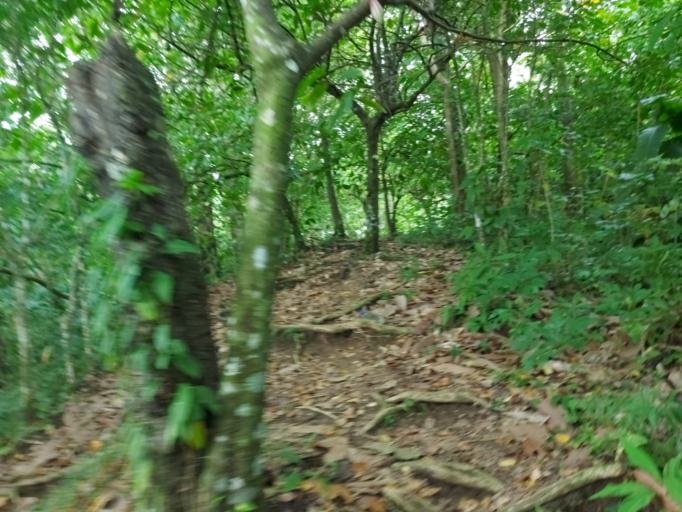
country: PA
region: Bocas del Toro
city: Barranco
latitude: 9.6403
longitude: -82.7837
